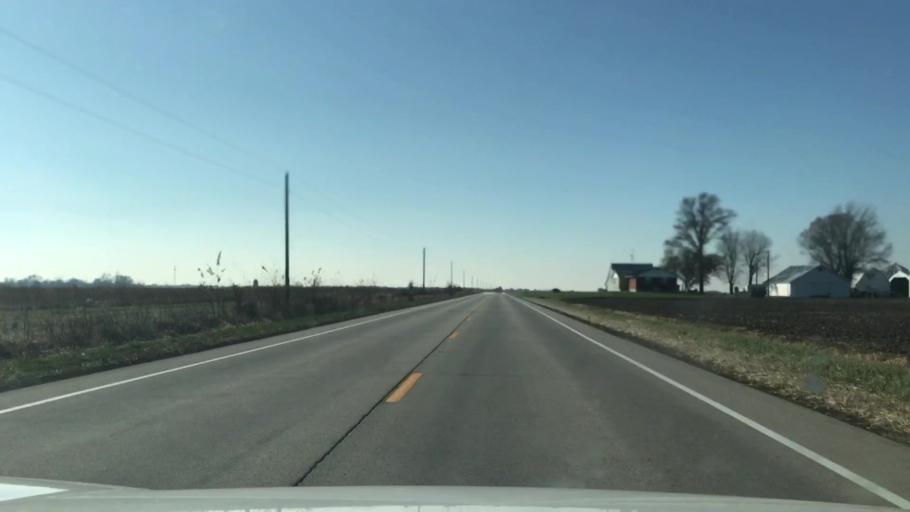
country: US
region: Illinois
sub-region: Washington County
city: Okawville
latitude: 38.4425
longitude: -89.5072
